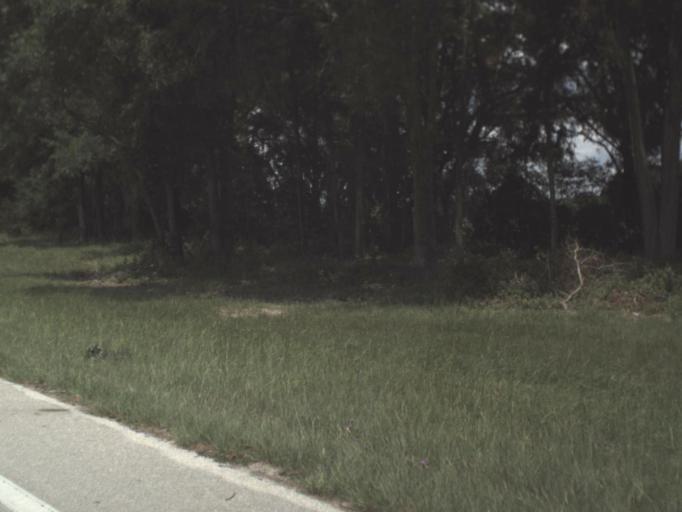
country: US
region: Florida
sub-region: Alachua County
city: Newberry
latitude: 29.6922
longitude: -82.6070
